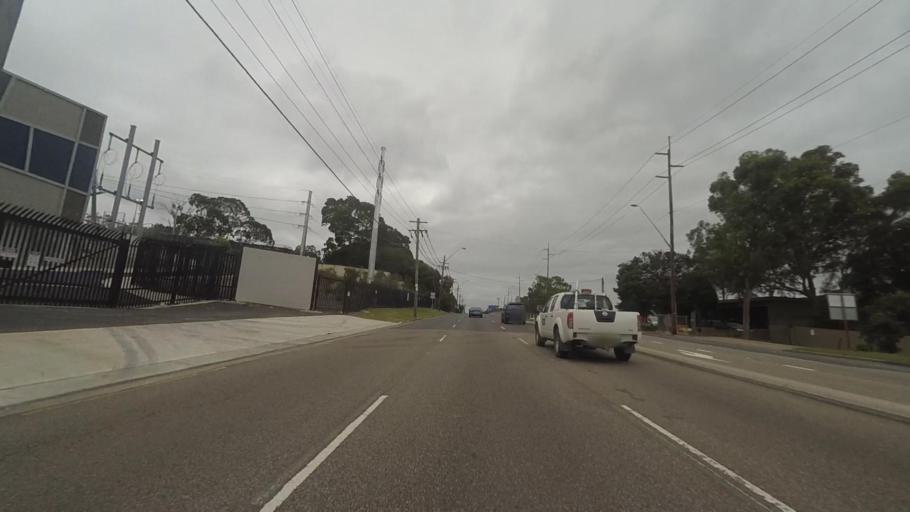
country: AU
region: New South Wales
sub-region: Auburn
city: Berala
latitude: -33.8942
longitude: 151.0381
